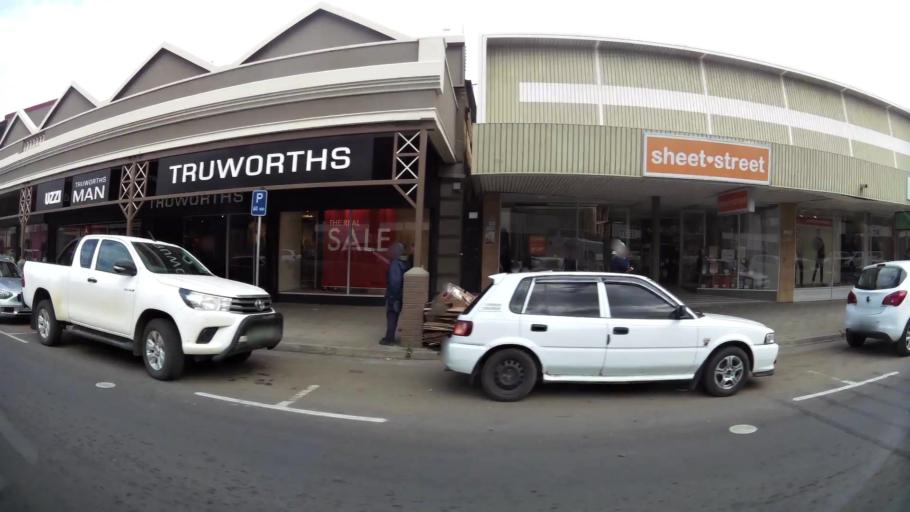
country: ZA
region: Orange Free State
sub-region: Fezile Dabi District Municipality
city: Kroonstad
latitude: -27.6643
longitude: 27.2339
